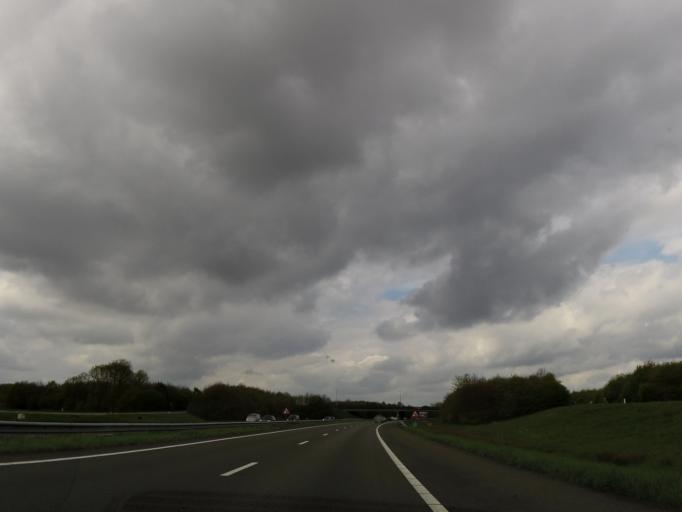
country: NL
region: Limburg
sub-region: Gemeente Weert
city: Weert
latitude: 51.2761
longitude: 5.6688
